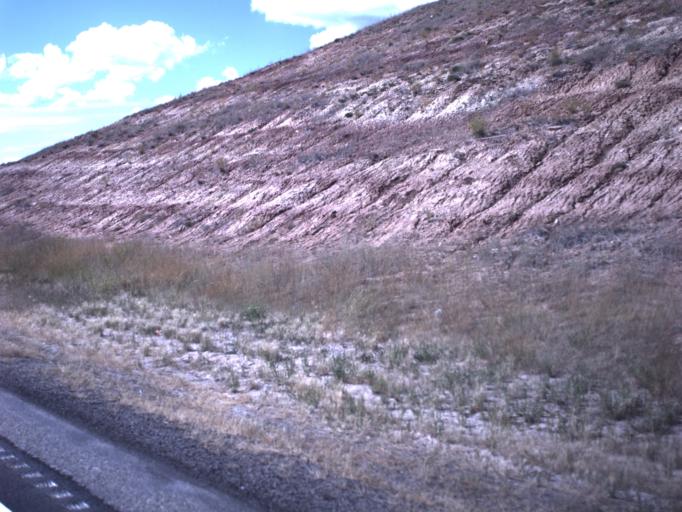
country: US
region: Utah
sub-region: Wasatch County
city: Heber
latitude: 40.1847
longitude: -111.0588
